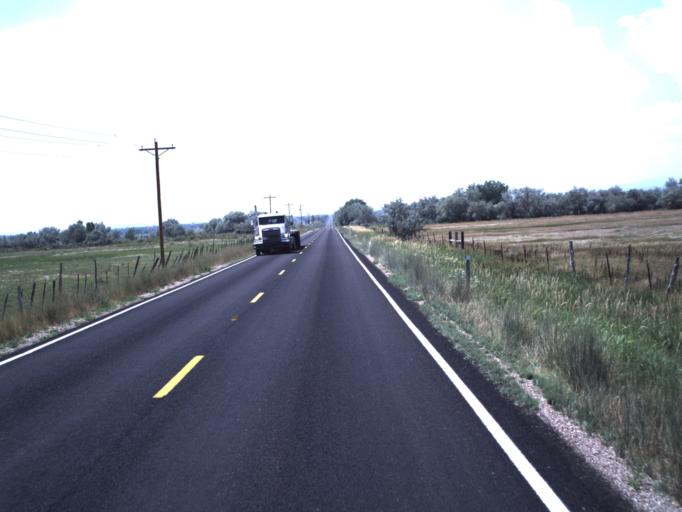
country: US
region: Utah
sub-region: Duchesne County
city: Roosevelt
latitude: 40.4037
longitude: -109.8282
